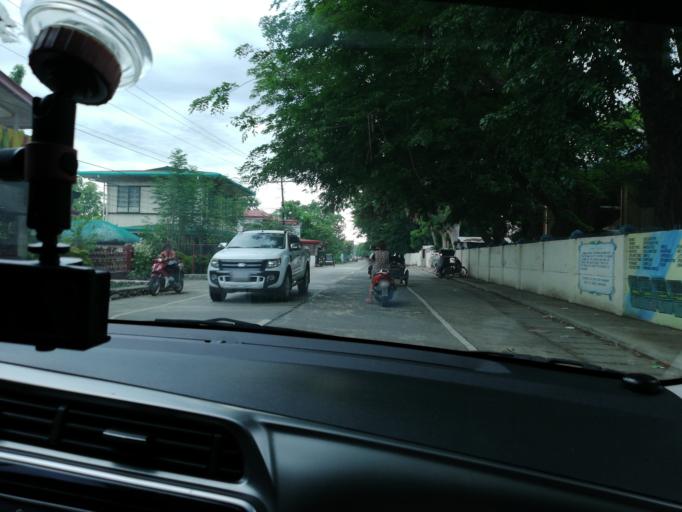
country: PH
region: Ilocos
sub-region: Province of Ilocos Sur
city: Narvacan
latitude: 17.4196
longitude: 120.4689
